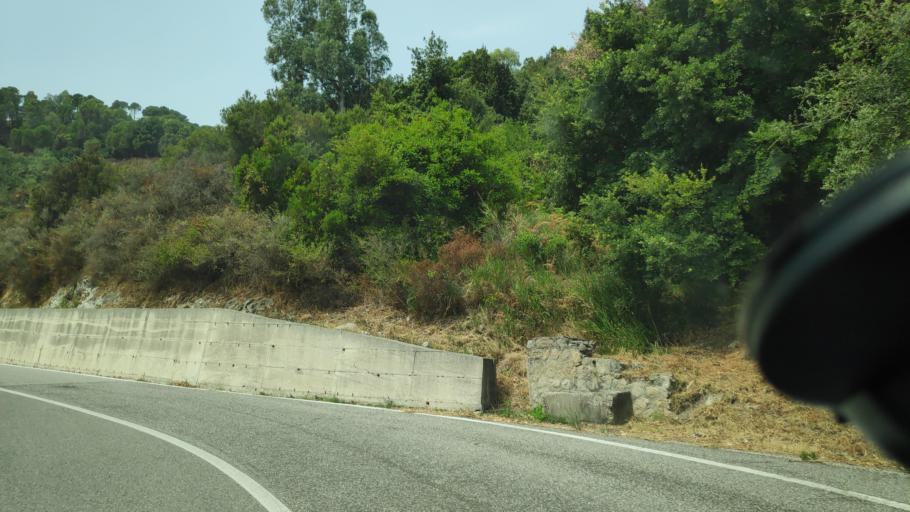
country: IT
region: Calabria
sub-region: Provincia di Catanzaro
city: San Sostene
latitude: 38.6407
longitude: 16.5097
